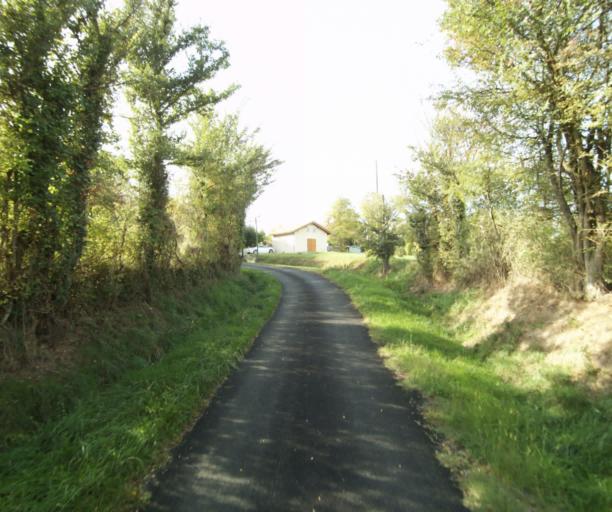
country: FR
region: Midi-Pyrenees
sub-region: Departement du Gers
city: Gondrin
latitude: 43.8882
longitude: 0.2409
